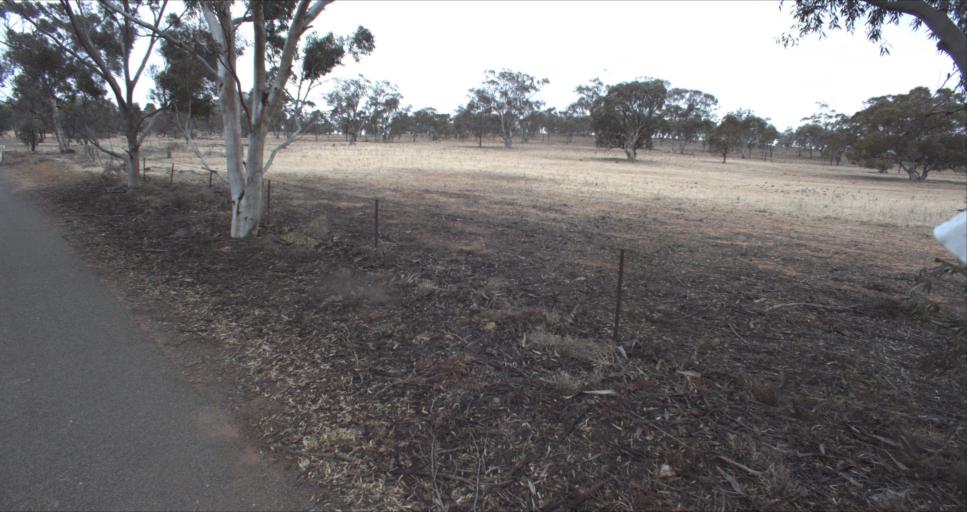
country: AU
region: New South Wales
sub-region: Leeton
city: Leeton
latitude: -34.4519
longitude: 146.3939
